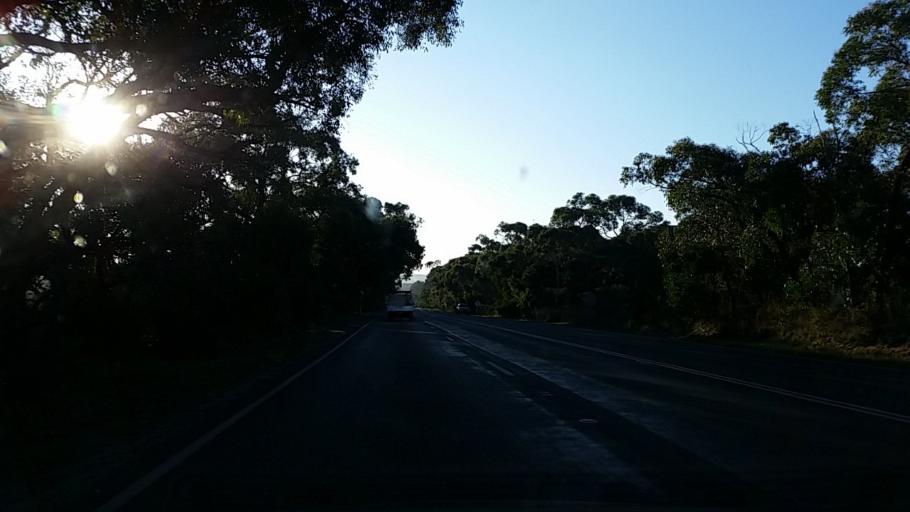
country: AU
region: South Australia
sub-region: Alexandrina
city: Mount Compass
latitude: -35.3314
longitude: 138.5892
